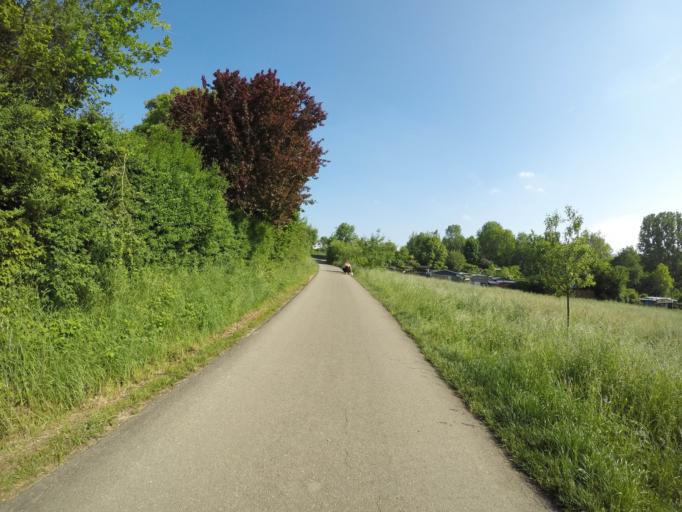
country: DE
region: Baden-Wuerttemberg
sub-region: Tuebingen Region
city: Reutlingen
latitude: 48.4812
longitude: 9.1796
